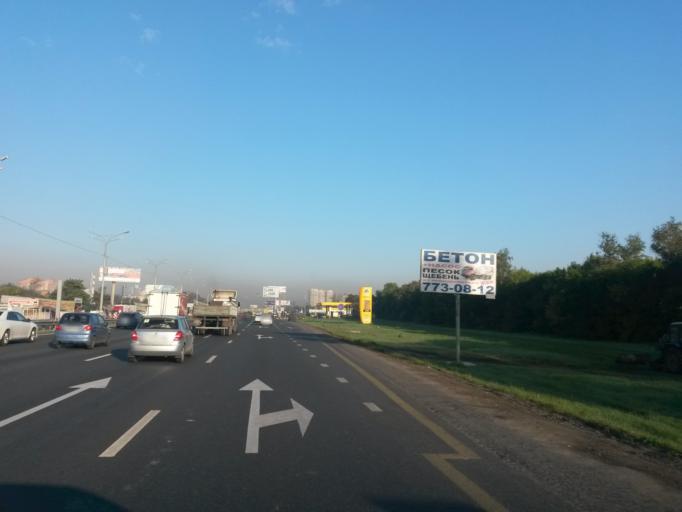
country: RU
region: Moskovskaya
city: Razvilka
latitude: 55.5841
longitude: 37.7436
